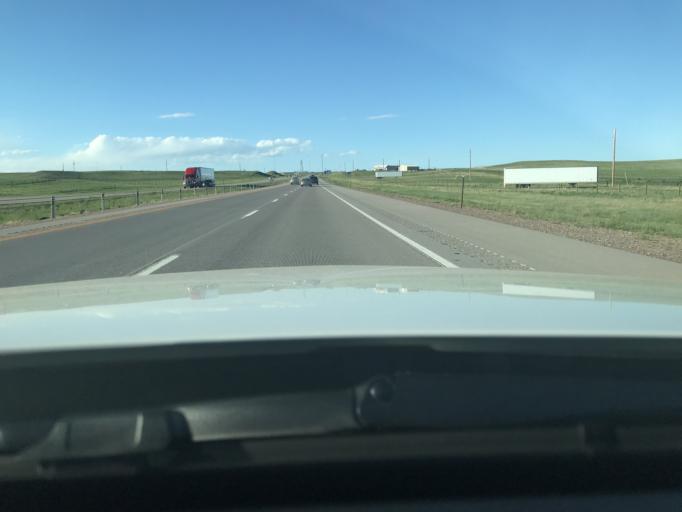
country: US
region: Wyoming
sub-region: Laramie County
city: South Greeley
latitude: 41.0248
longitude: -104.9017
